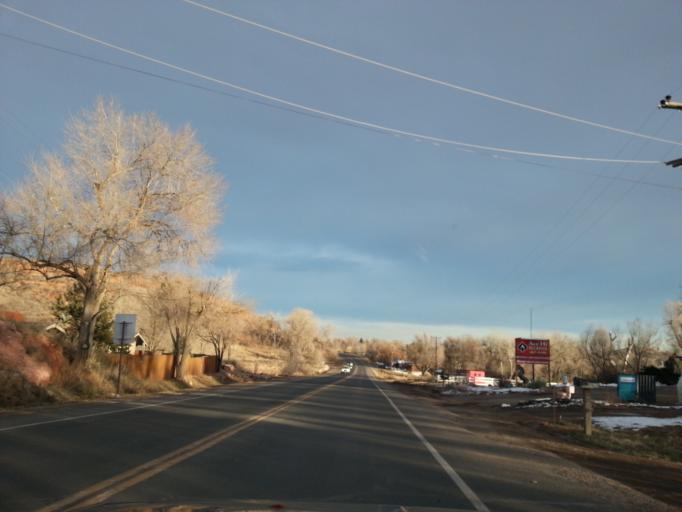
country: US
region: Colorado
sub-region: Larimer County
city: Loveland
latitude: 40.4072
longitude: -105.1475
